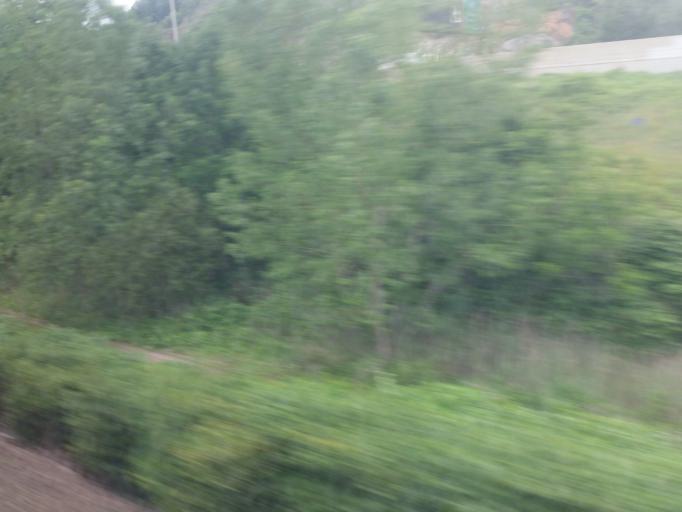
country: US
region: New Jersey
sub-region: Hudson County
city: Jersey City
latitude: 40.7582
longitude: -74.0833
